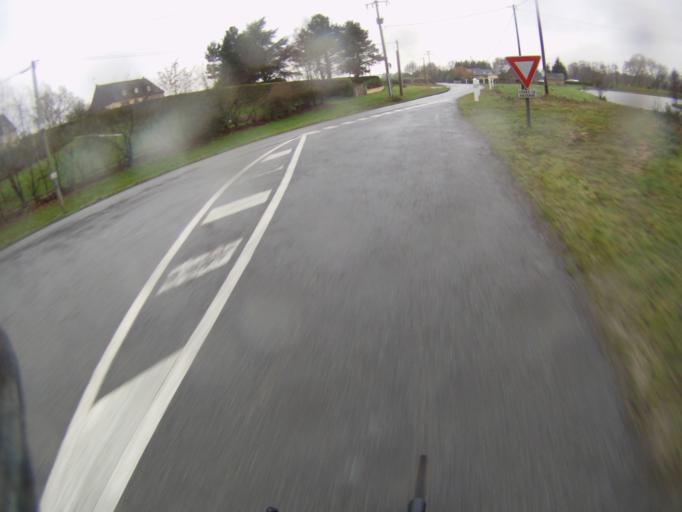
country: FR
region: Brittany
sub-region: Departement d'Ille-et-Vilaine
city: Chanteloup
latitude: 47.9377
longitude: -1.6039
